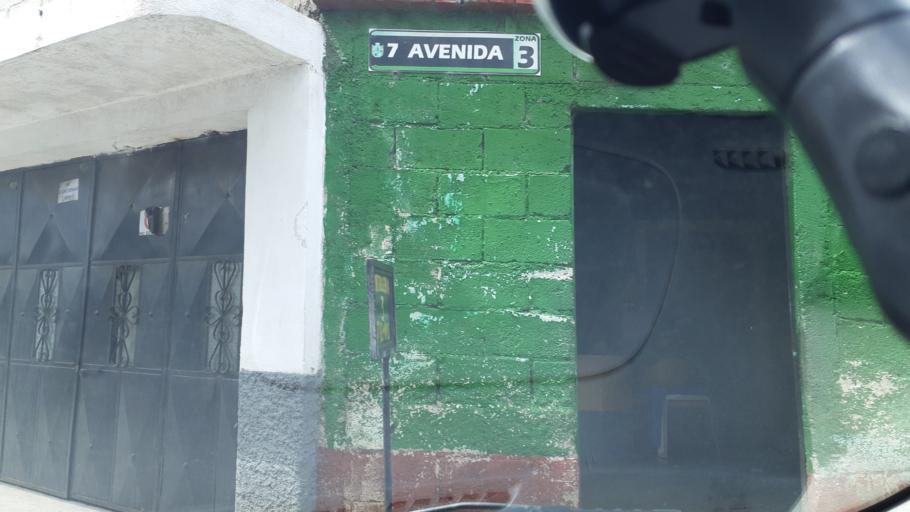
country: GT
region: Chimaltenango
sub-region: Municipio de Chimaltenango
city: Chimaltenango
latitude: 14.6641
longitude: -90.8255
